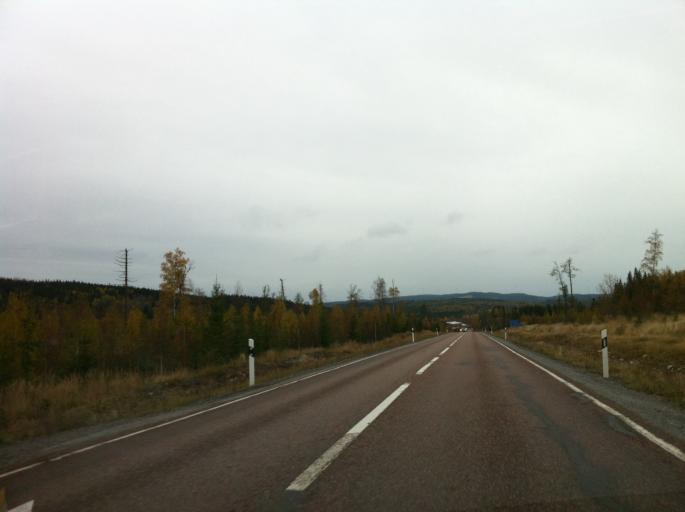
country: SE
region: Dalarna
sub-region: Ludvika Kommun
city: Grangesberg
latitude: 60.0191
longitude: 14.9834
